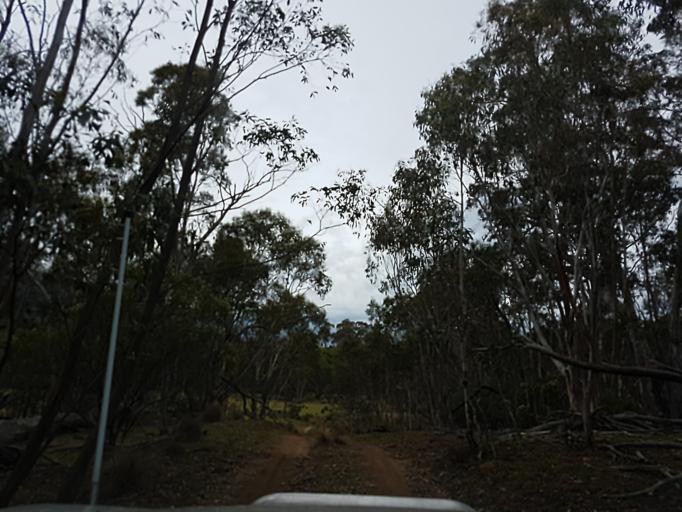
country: AU
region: New South Wales
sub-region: Snowy River
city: Jindabyne
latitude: -36.8525
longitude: 148.2583
